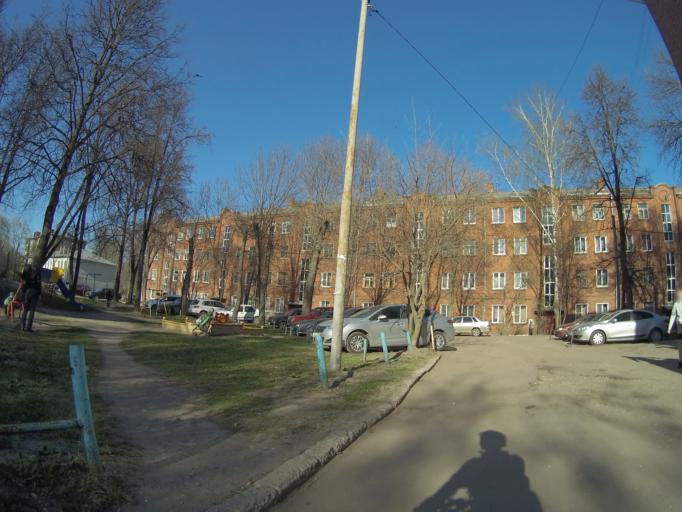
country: RU
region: Vladimir
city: Vladimir
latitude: 56.1496
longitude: 40.4212
